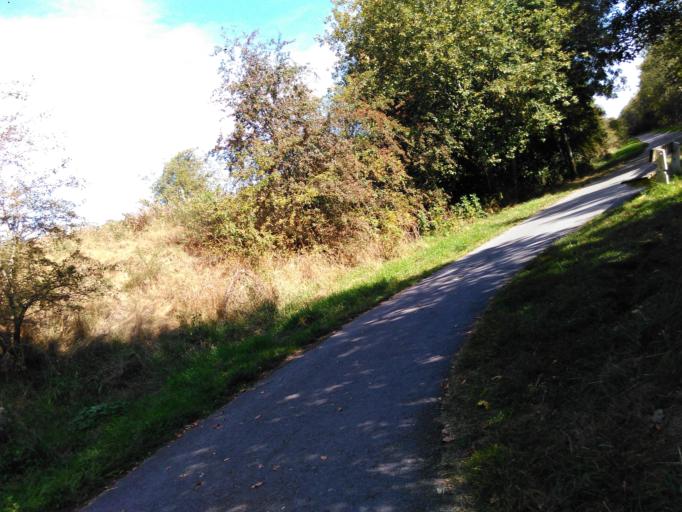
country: BE
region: Wallonia
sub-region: Province du Luxembourg
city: Bastogne
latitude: 50.0089
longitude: 5.7289
